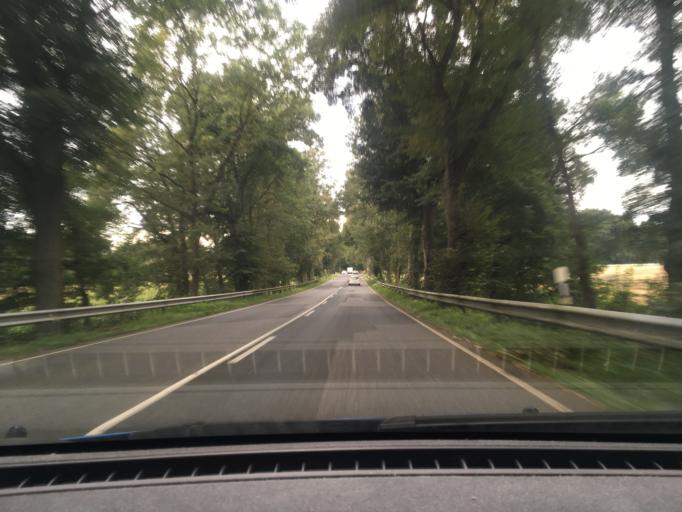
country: DE
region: Lower Saxony
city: Unterluss
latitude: 52.7810
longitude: 10.3447
